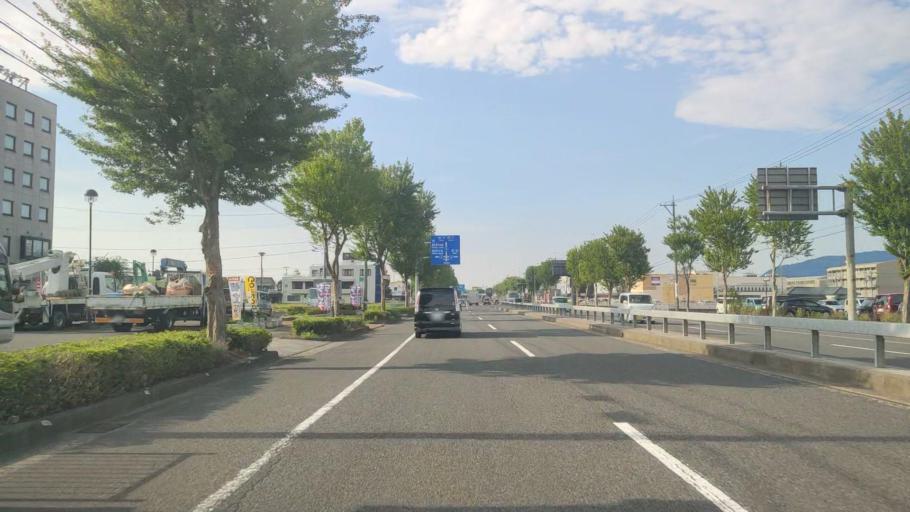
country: JP
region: Fukui
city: Takefu
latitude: 35.9043
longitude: 136.1921
